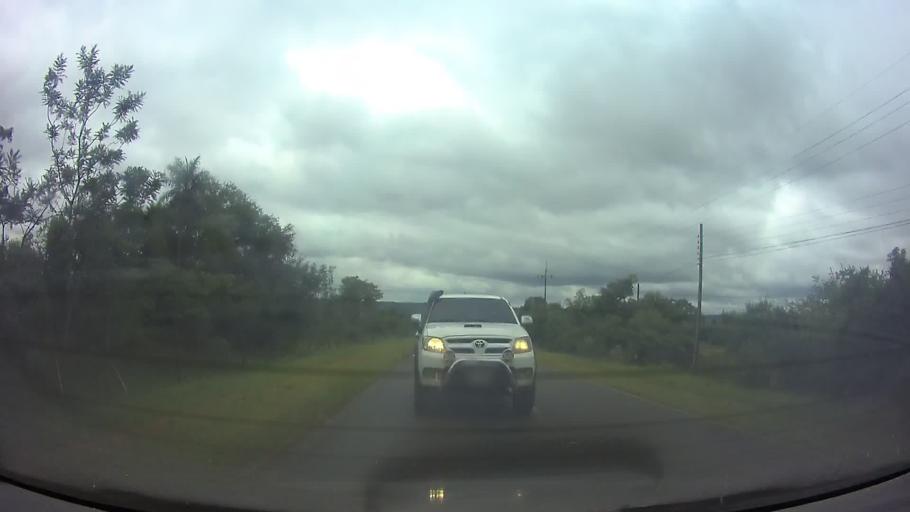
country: PY
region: Central
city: Guarambare
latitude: -25.5158
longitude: -57.4900
